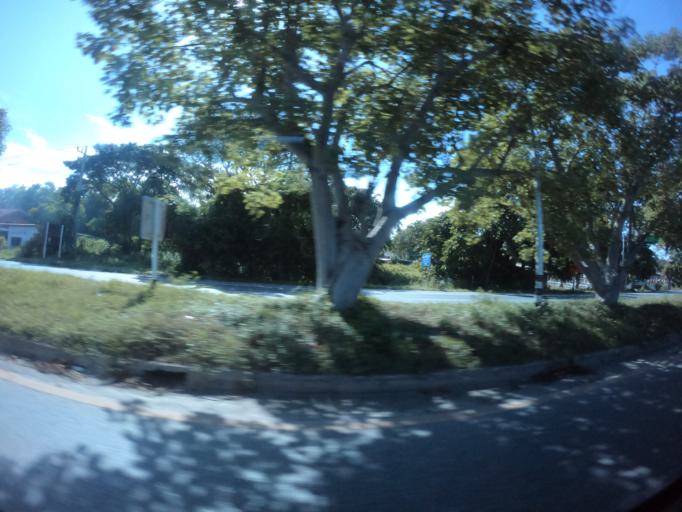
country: TH
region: Nakhon Nayok
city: Ban Na
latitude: 14.2092
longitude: 101.0688
